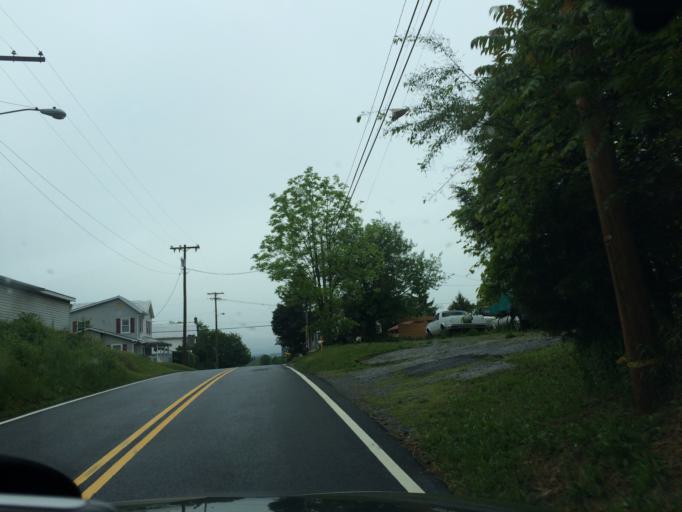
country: US
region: Maryland
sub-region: Frederick County
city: Woodsboro
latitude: 39.6053
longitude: -77.3177
